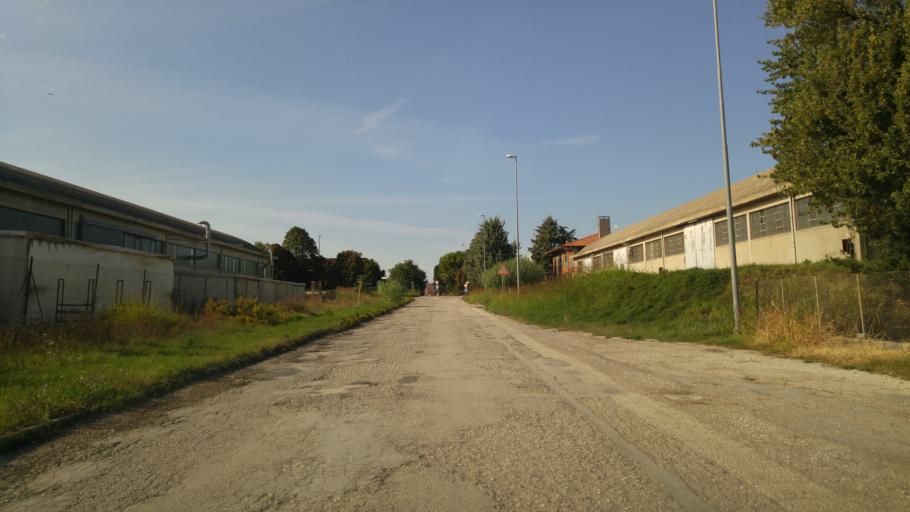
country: IT
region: The Marches
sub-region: Provincia di Pesaro e Urbino
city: Bellocchi
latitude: 43.7968
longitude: 13.0146
